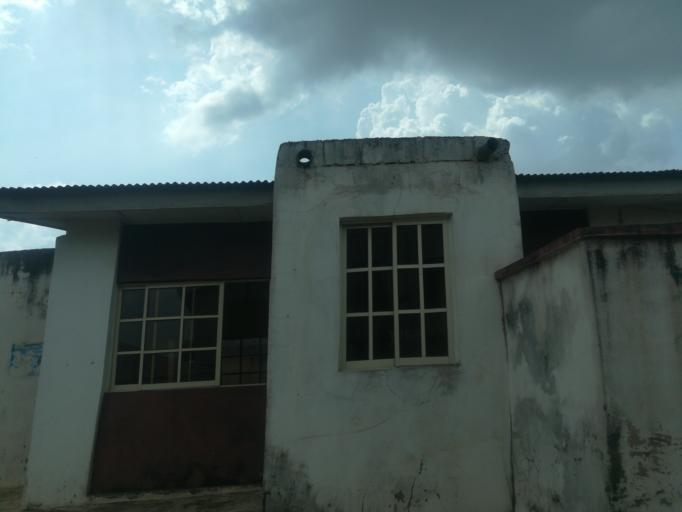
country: NG
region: Oyo
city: Ibadan
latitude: 7.4393
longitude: 3.9405
